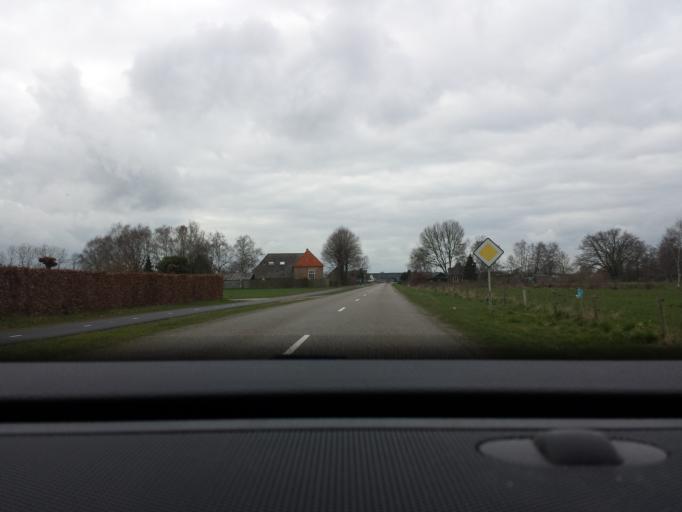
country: NL
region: Gelderland
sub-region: Gemeente Bronckhorst
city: Hengelo
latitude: 52.0322
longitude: 6.3163
